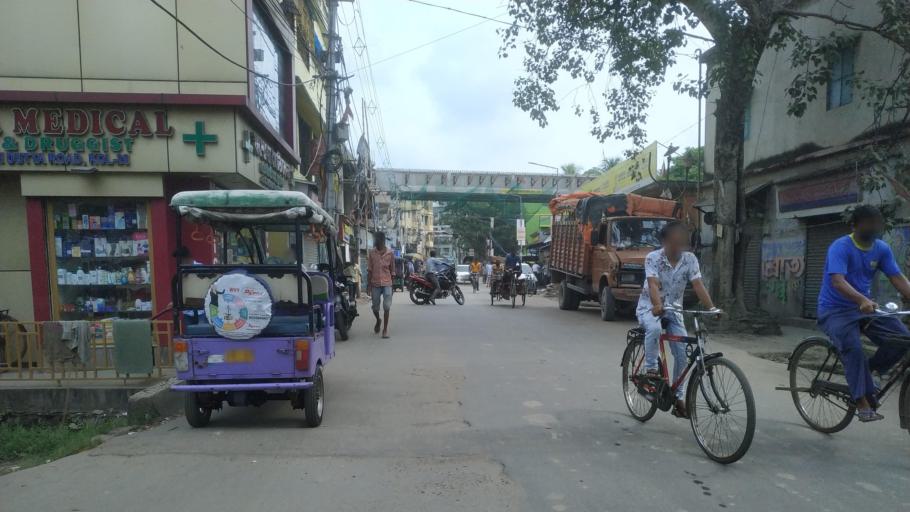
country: IN
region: West Bengal
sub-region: North 24 Parganas
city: Dam Dam
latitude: 22.6392
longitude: 88.4154
